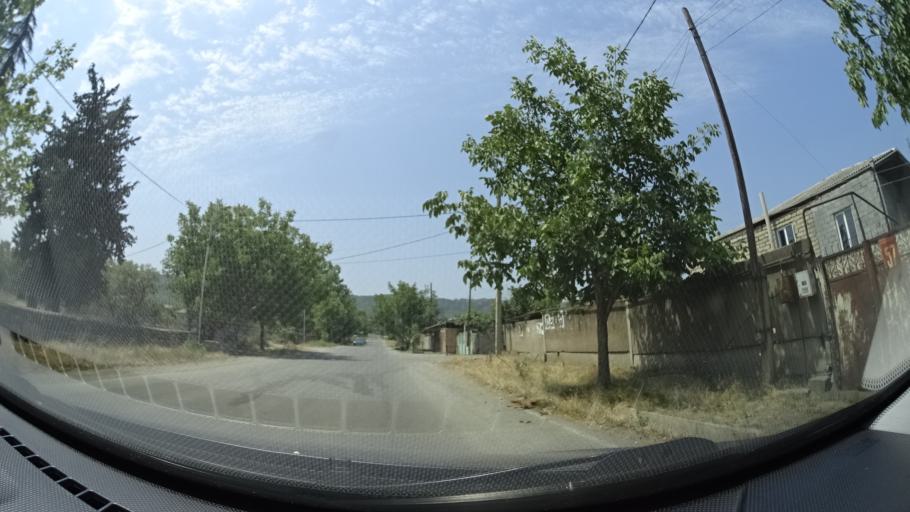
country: GE
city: Tsnori
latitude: 41.6209
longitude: 45.9664
